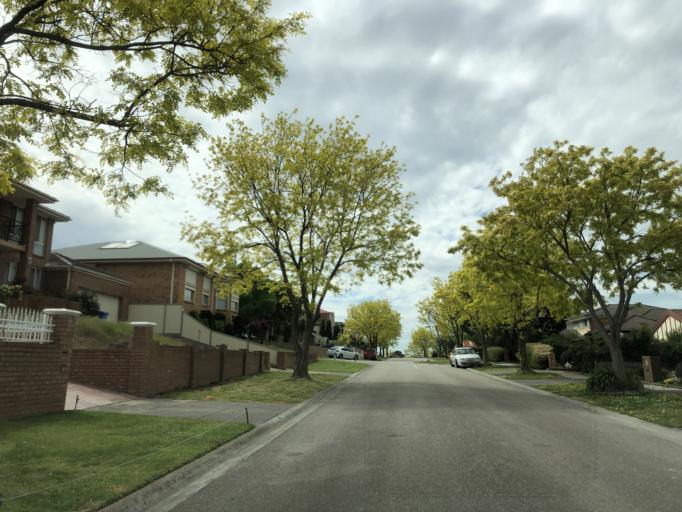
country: AU
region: Victoria
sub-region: Casey
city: Endeavour Hills
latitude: -37.9775
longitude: 145.2617
